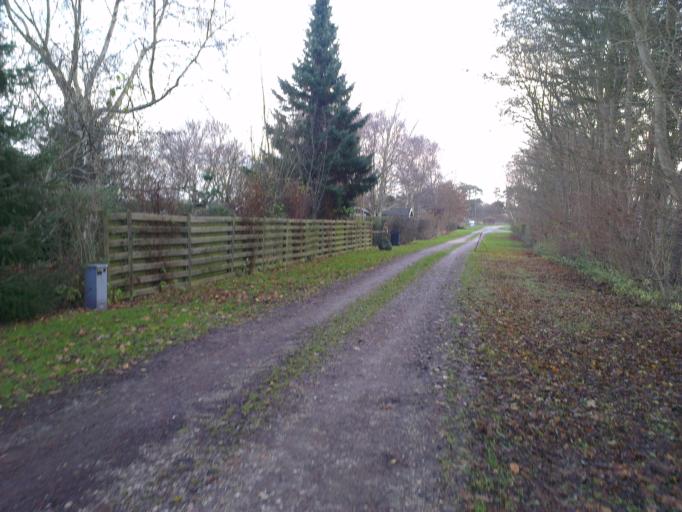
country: DK
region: Capital Region
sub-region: Frederikssund Kommune
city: Jaegerspris
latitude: 55.8417
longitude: 11.9590
